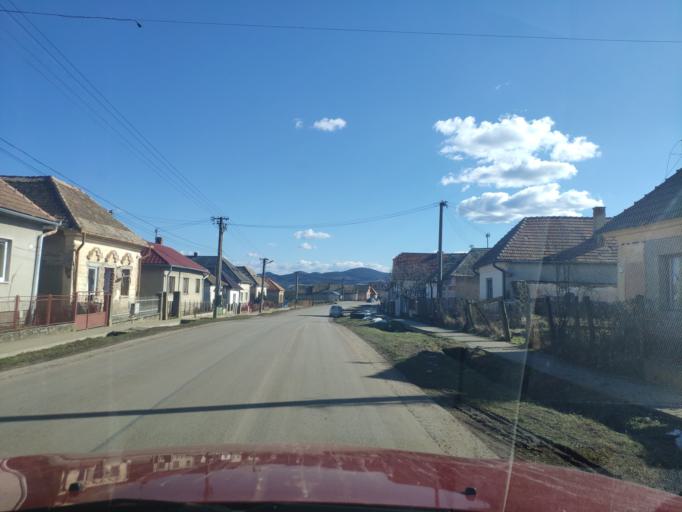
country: SK
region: Banskobystricky
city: Rimavska Sobota
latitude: 48.2873
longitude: 20.0914
